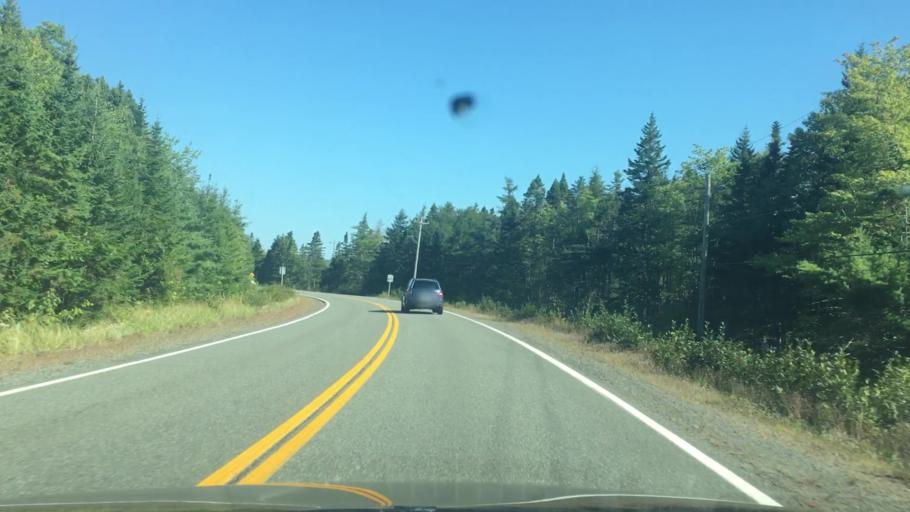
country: CA
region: Nova Scotia
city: Cole Harbour
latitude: 44.8018
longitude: -62.8805
